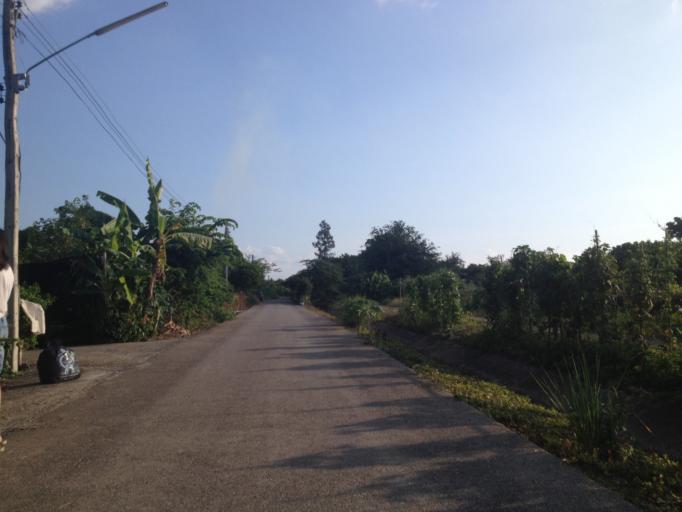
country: TH
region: Chiang Mai
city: Hang Dong
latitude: 18.6850
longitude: 98.9009
